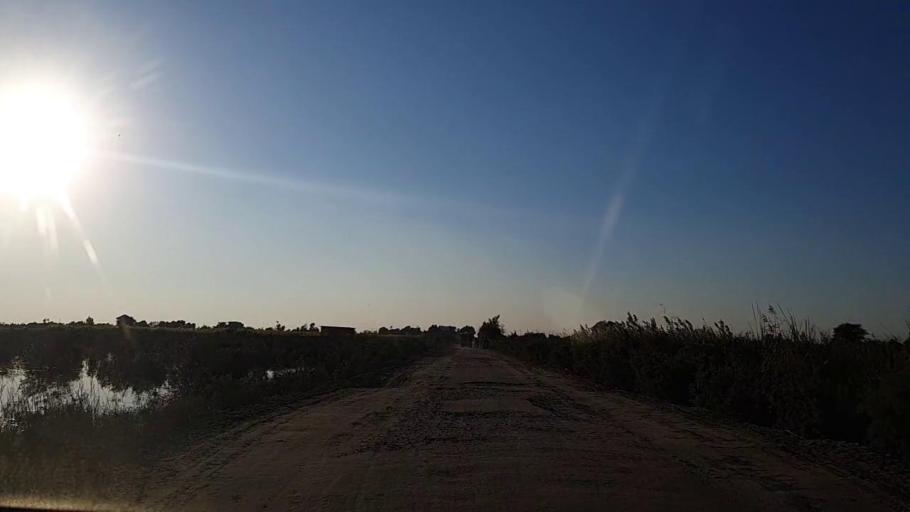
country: PK
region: Sindh
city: Khadro
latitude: 26.2790
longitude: 68.8363
